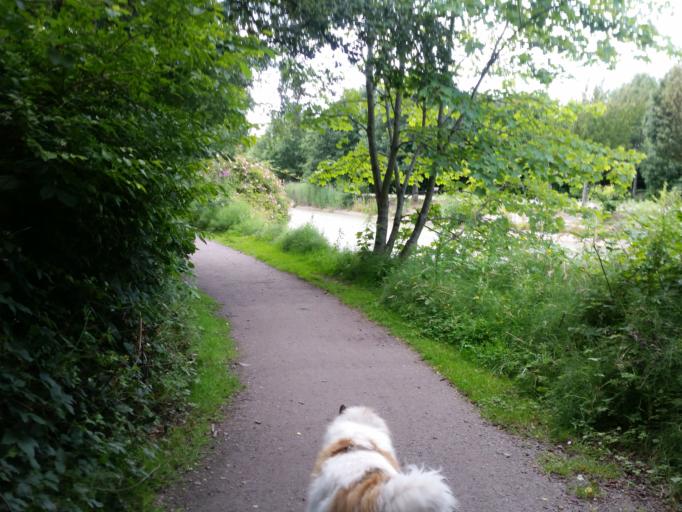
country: GB
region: Northern Ireland
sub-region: Castlereagh District
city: Castlereagh
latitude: 54.6088
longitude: -5.8827
